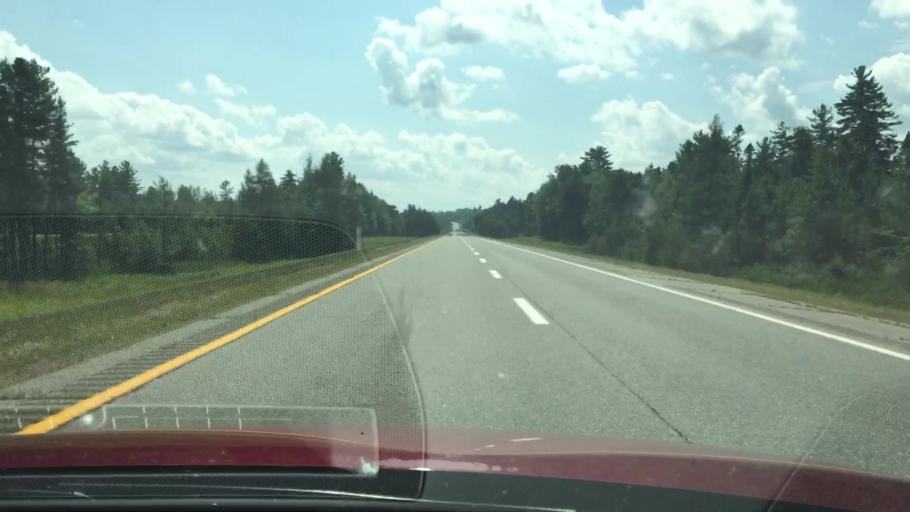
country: US
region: Maine
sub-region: Penobscot County
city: Lincoln
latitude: 45.4746
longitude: -68.5784
